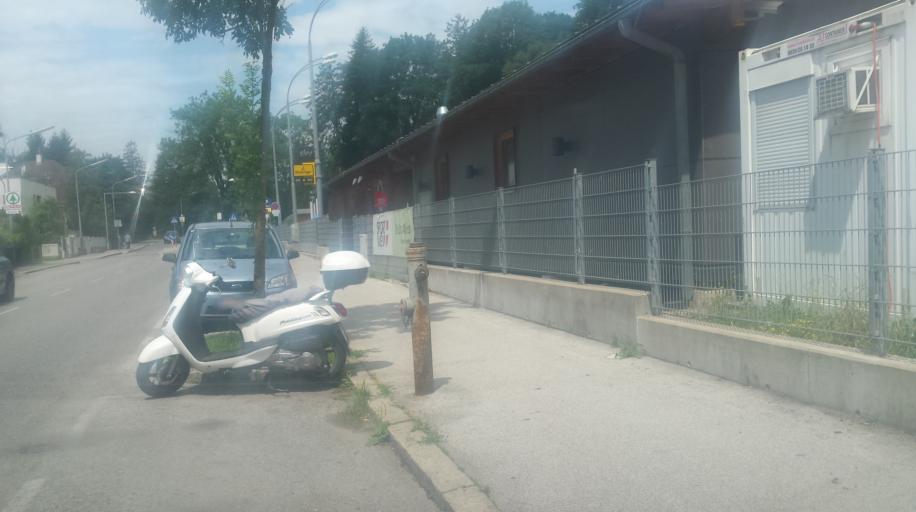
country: AT
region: Lower Austria
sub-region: Politischer Bezirk Wien-Umgebung
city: Purkersdorf
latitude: 48.2292
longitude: 16.2026
